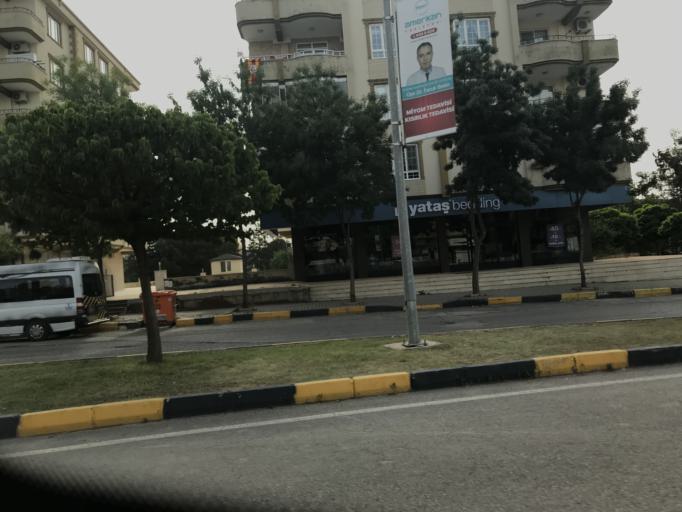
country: TR
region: Gaziantep
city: Sehitkamil
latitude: 37.0706
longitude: 37.3393
